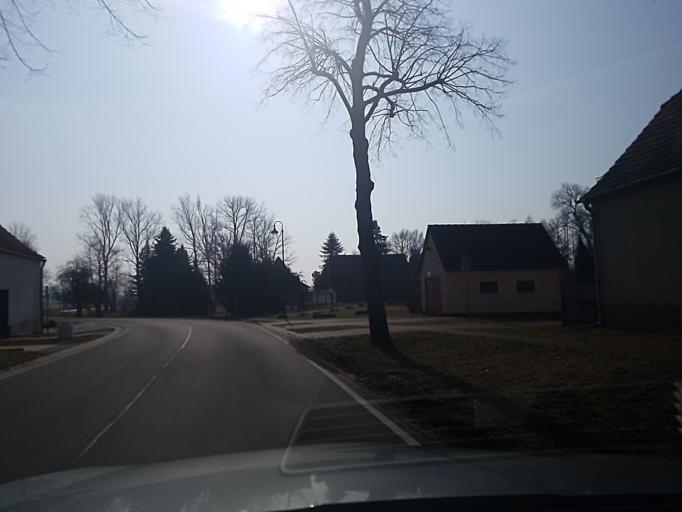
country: DE
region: Brandenburg
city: Falkenberg
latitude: 51.6416
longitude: 13.2659
